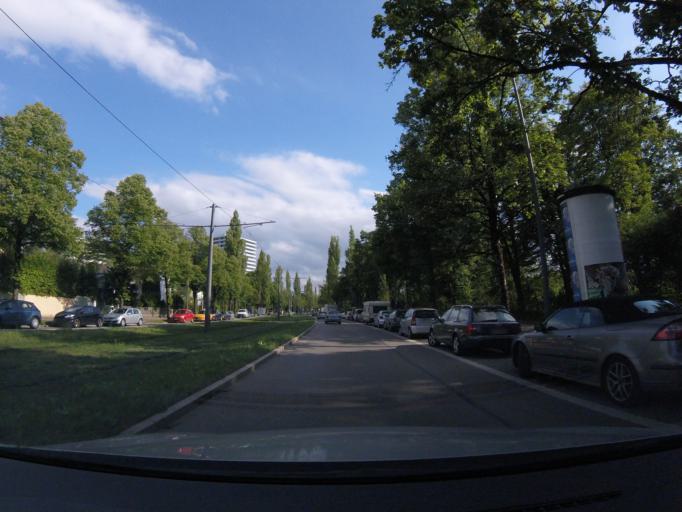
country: DE
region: Bavaria
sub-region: Upper Bavaria
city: Bogenhausen
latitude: 48.1578
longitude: 11.6290
